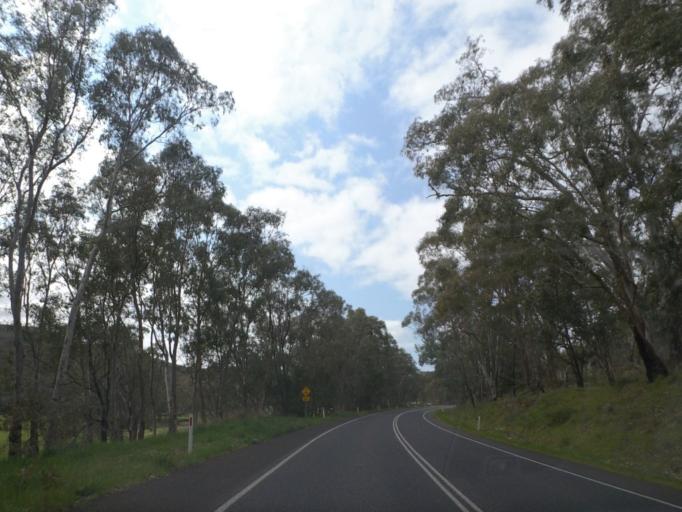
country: AU
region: Victoria
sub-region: Murrindindi
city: Kinglake West
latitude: -37.1403
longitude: 145.2611
